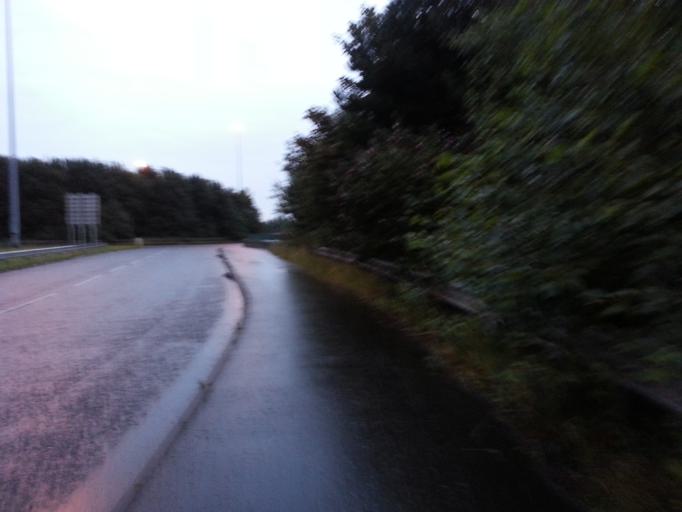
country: GB
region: Northern Ireland
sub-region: Newtownabbey District
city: Newtownabbey
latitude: 54.6297
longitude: -5.9216
